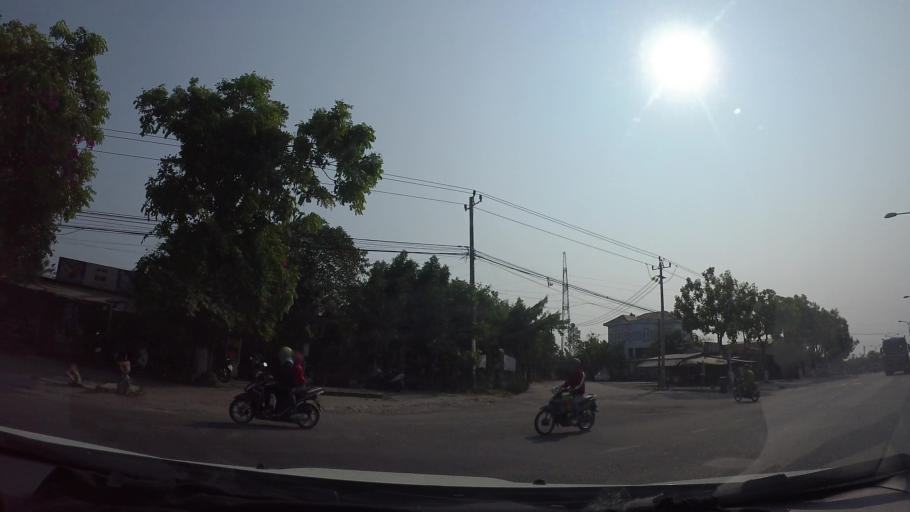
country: VN
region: Da Nang
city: Cam Le
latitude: 16.0127
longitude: 108.1811
